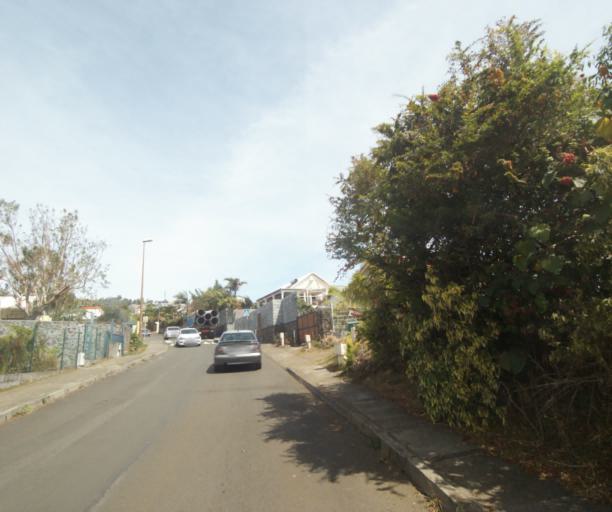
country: RE
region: Reunion
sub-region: Reunion
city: Saint-Paul
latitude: -21.0369
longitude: 55.3092
